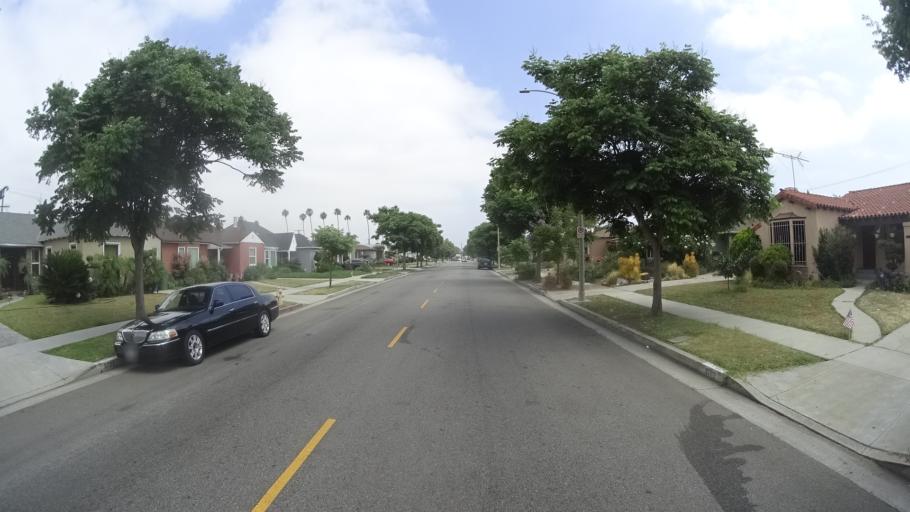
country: US
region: California
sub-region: Los Angeles County
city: View Park-Windsor Hills
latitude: 34.0197
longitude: -118.3403
